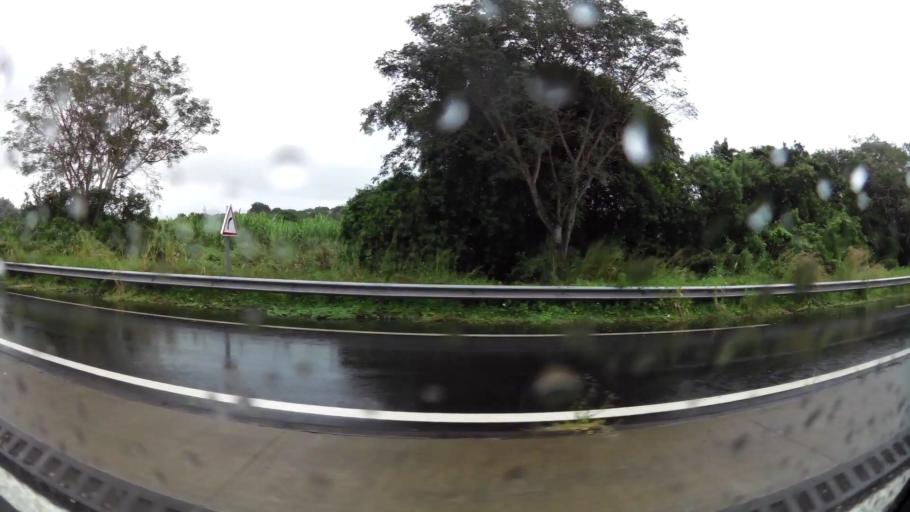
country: RE
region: Reunion
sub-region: Reunion
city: Saint-Benoit
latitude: -21.0266
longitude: 55.7047
